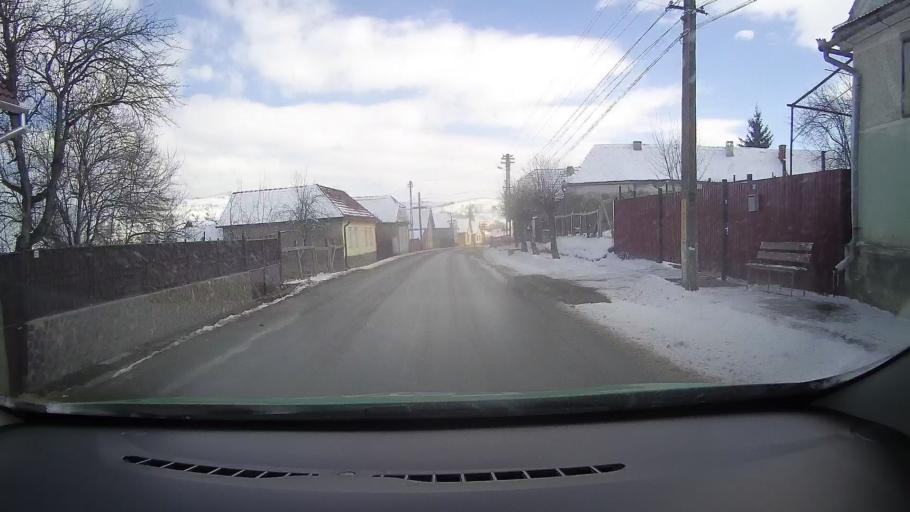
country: RO
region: Sibiu
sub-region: Comuna Barghis
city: Barghis
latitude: 45.9822
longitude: 24.5348
